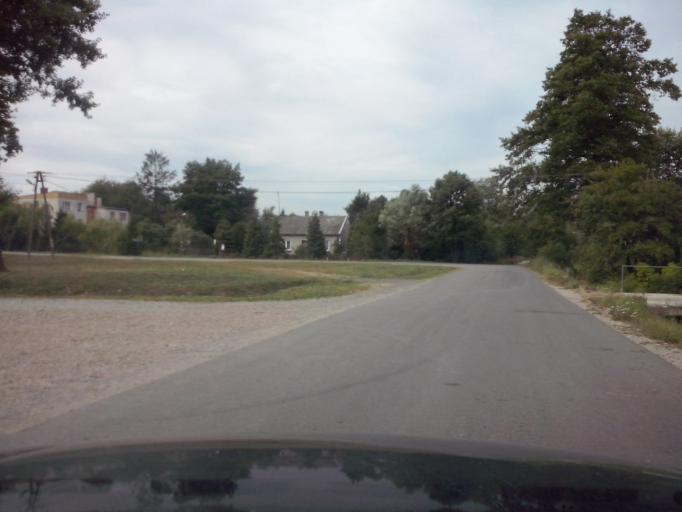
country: PL
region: Swietokrzyskie
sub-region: Powiat kielecki
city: Lagow
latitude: 50.7356
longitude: 21.0424
